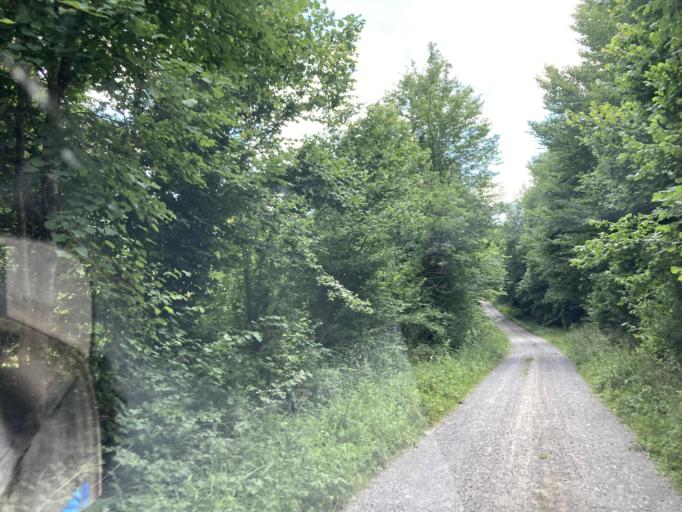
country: DE
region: Baden-Wuerttemberg
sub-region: Tuebingen Region
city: Ofterdingen
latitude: 48.4459
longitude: 9.0222
